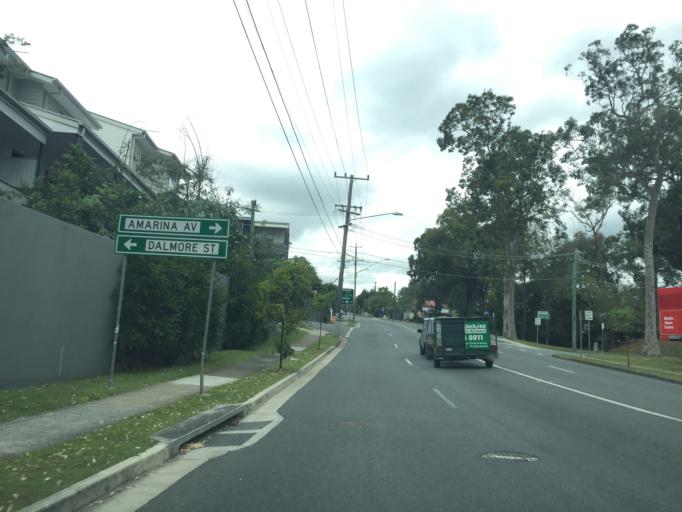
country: AU
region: Queensland
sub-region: Brisbane
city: Wilston
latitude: -27.4418
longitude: 152.9903
